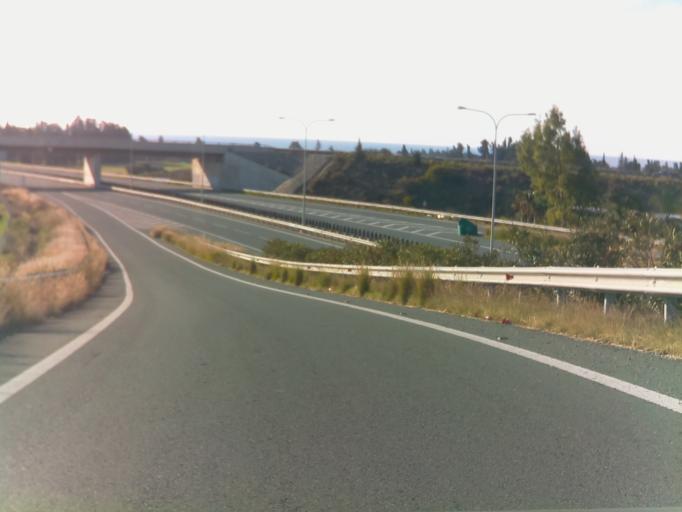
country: CY
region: Pafos
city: Paphos
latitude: 34.7238
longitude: 32.5305
